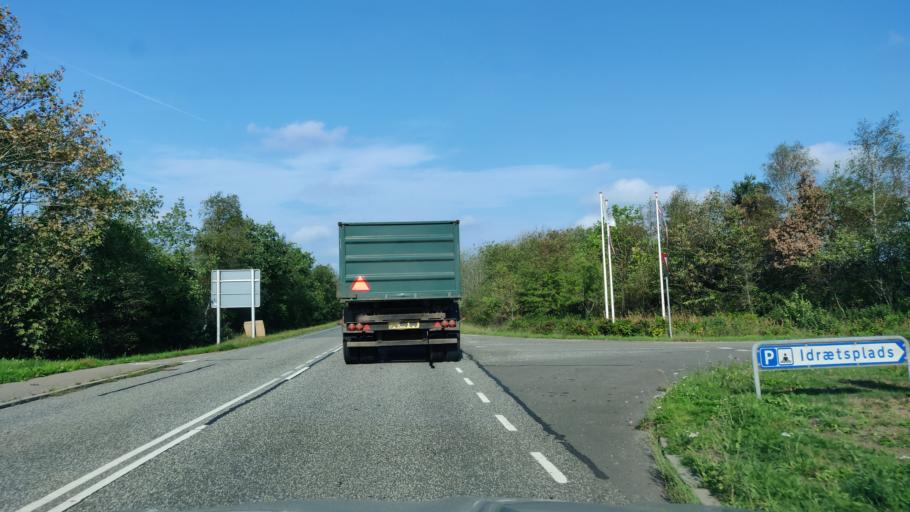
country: DK
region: Central Jutland
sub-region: Herning Kommune
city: Sunds
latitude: 56.2418
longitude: 9.0874
